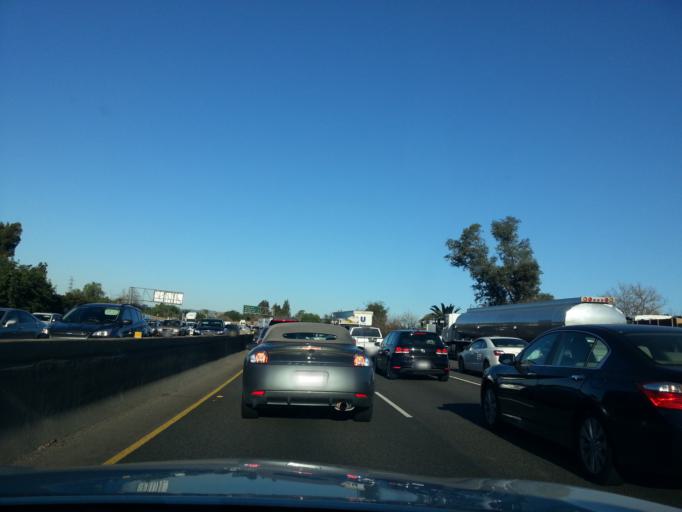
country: US
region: California
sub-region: Los Angeles County
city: Northridge
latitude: 34.1729
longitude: -118.5343
